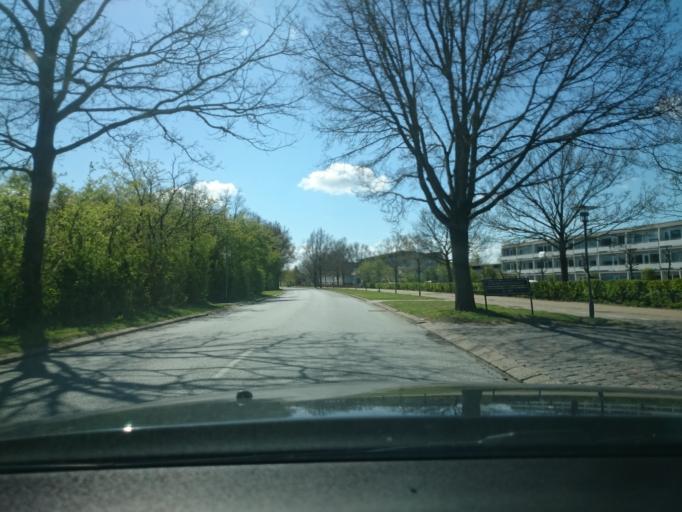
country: DK
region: Capital Region
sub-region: Lyngby-Tarbaek Kommune
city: Kongens Lyngby
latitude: 55.7913
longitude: 12.5340
